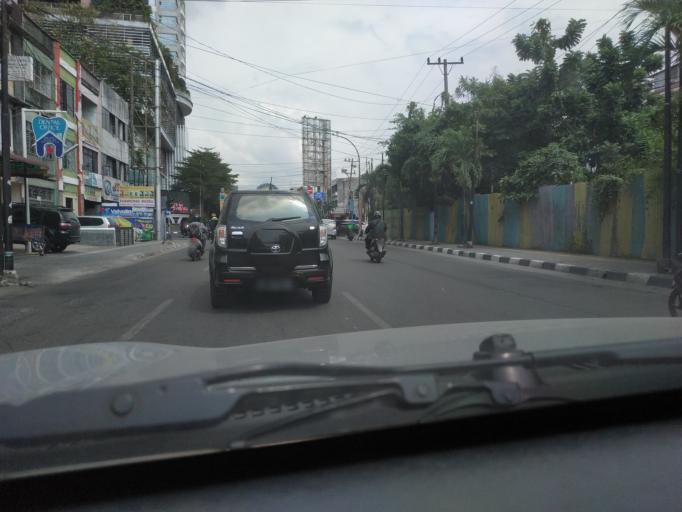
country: ID
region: North Sumatra
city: Medan
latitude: 3.5842
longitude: 98.6664
